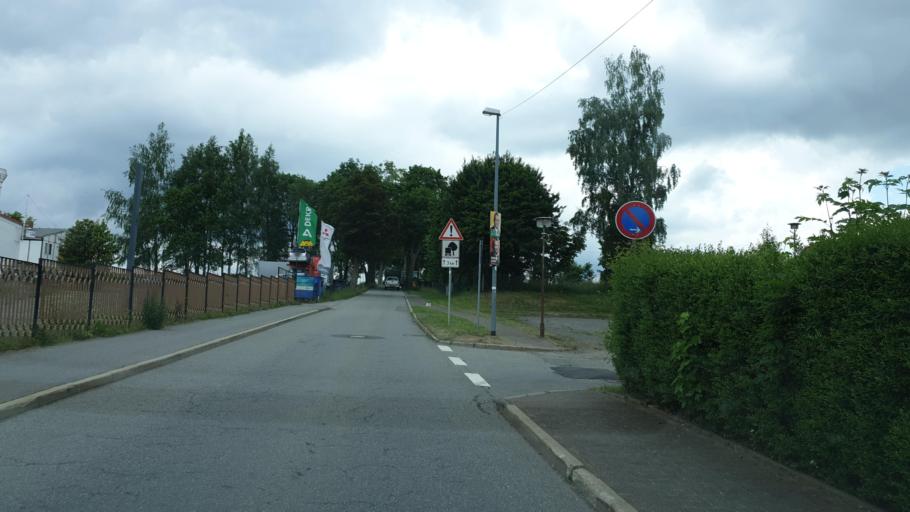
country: DE
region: Saxony
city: Marienberg
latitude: 50.6803
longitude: 13.1781
